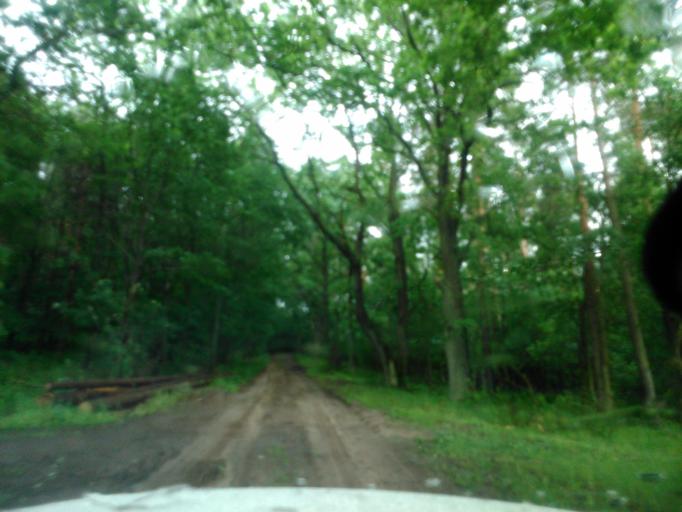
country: PL
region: Pomeranian Voivodeship
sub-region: Powiat slupski
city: Smoldzino
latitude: 54.6383
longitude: 17.2726
